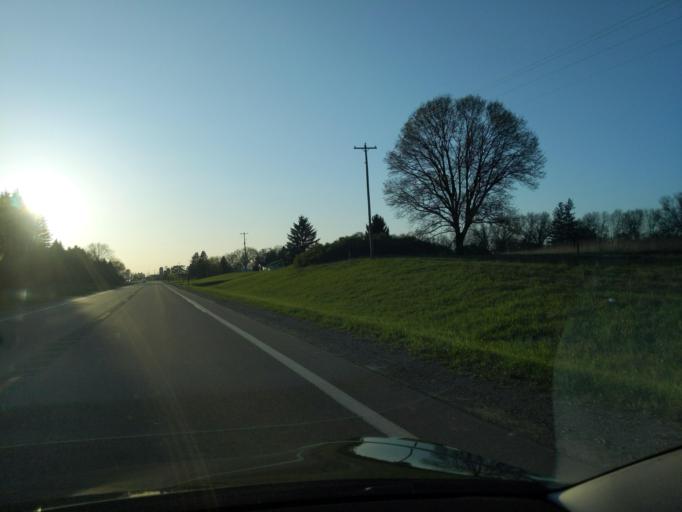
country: US
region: Michigan
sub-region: Ingham County
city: Stockbridge
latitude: 42.4143
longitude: -84.1388
